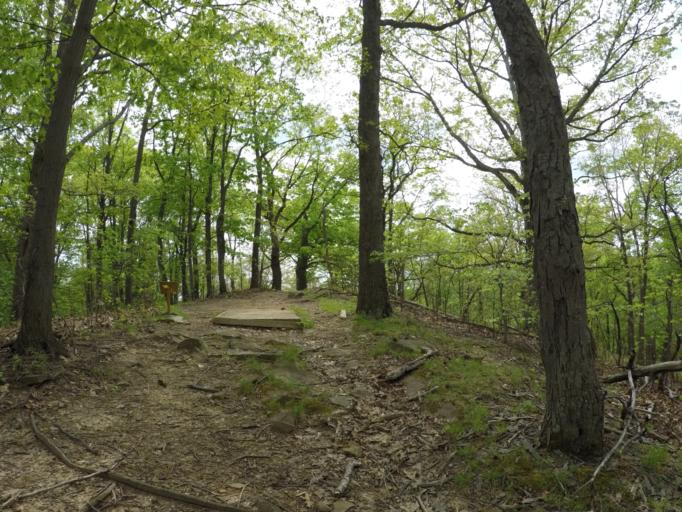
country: US
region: West Virginia
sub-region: Cabell County
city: Huntington
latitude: 38.4174
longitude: -82.3926
